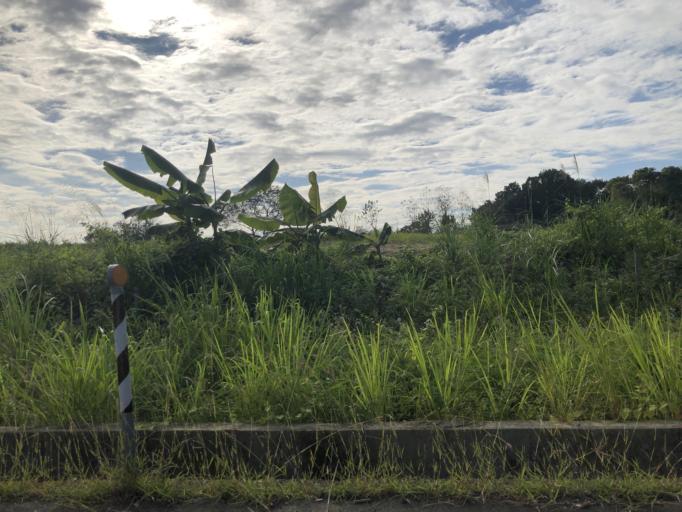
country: TW
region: Taiwan
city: Yujing
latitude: 23.0437
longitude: 120.4226
